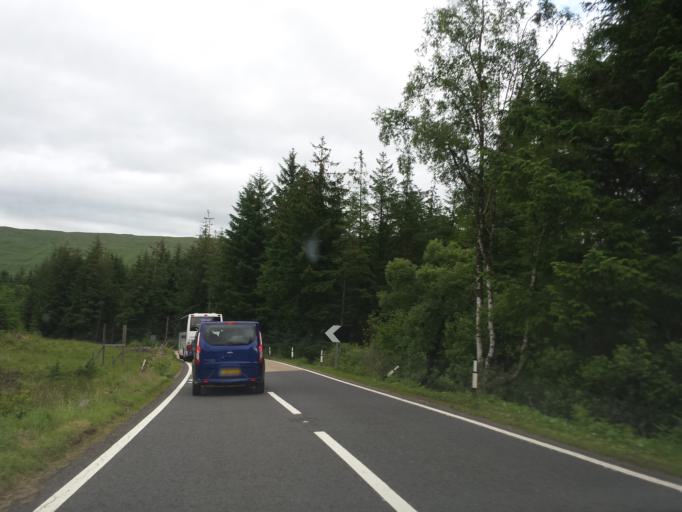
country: GB
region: Scotland
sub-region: Stirling
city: Callander
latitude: 56.4391
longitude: -4.3528
